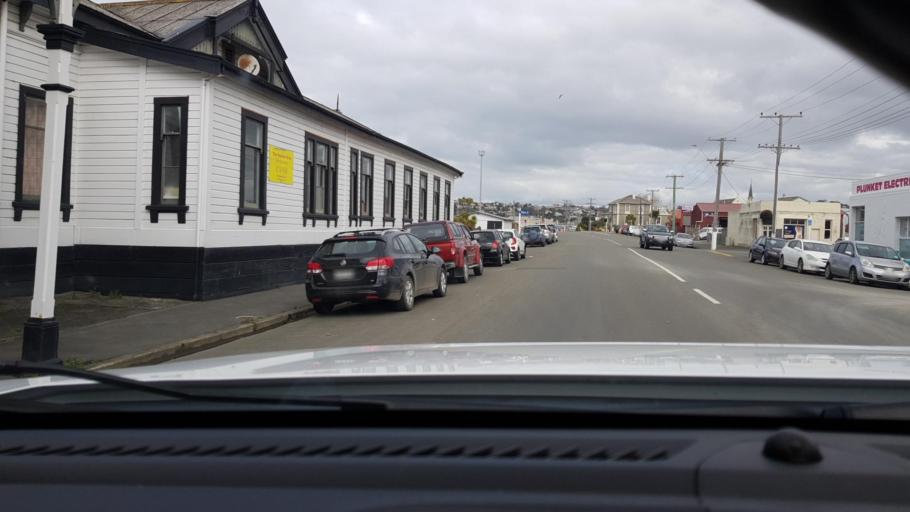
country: NZ
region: Otago
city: Oamaru
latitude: -45.0957
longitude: 170.9750
